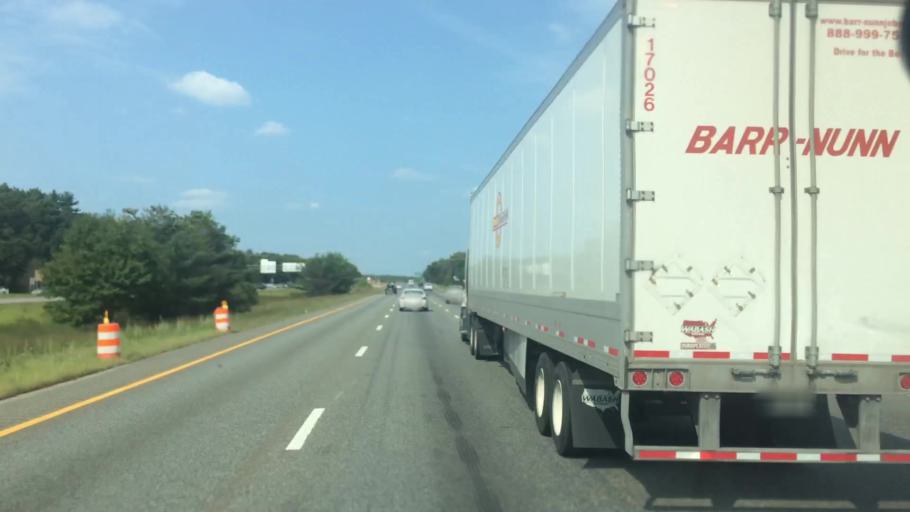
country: US
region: Massachusetts
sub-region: Bristol County
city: Attleboro
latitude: 41.9561
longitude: -71.3041
